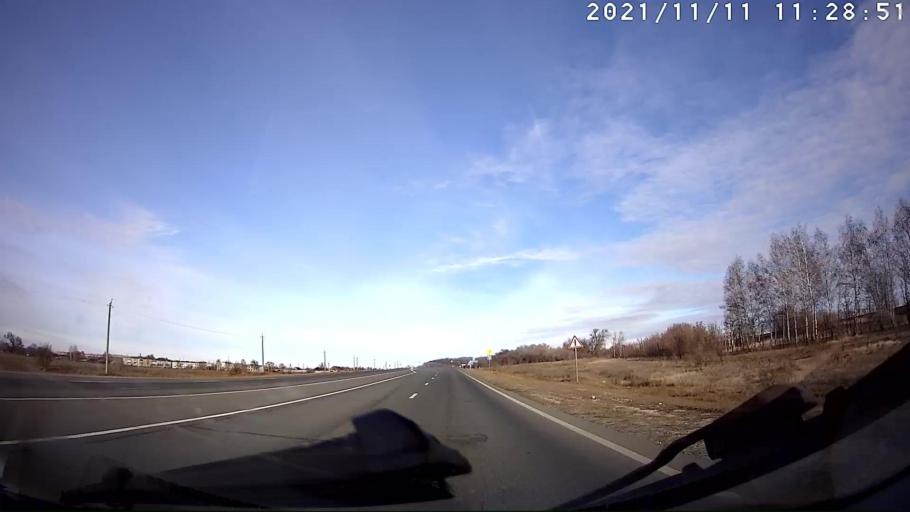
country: RU
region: Samara
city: Varlamovo
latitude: 53.2660
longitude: 48.4805
